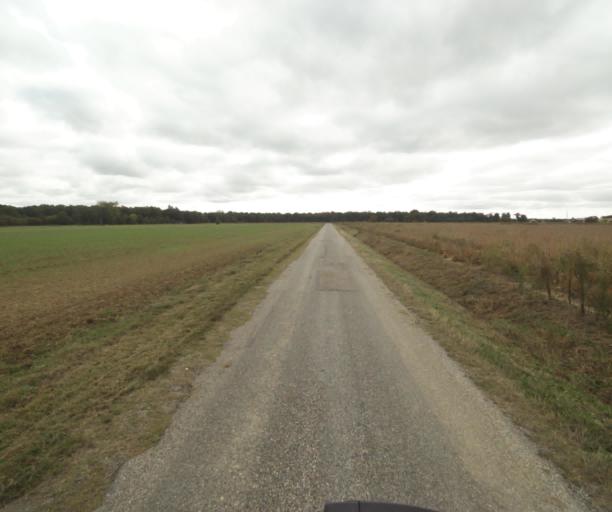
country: FR
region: Midi-Pyrenees
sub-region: Departement du Tarn-et-Garonne
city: Montech
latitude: 43.9617
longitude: 1.2543
